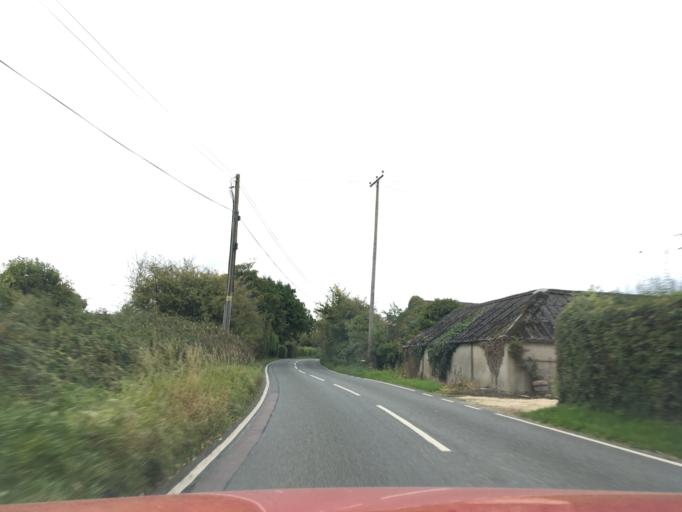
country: GB
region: England
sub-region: Gloucestershire
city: Stonehouse
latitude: 51.7598
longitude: -2.3154
